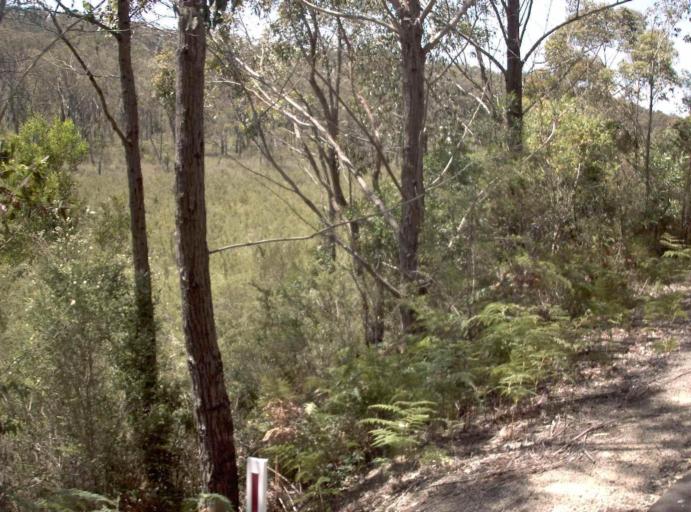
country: AU
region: Victoria
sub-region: East Gippsland
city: Lakes Entrance
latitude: -37.7110
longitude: 148.6742
